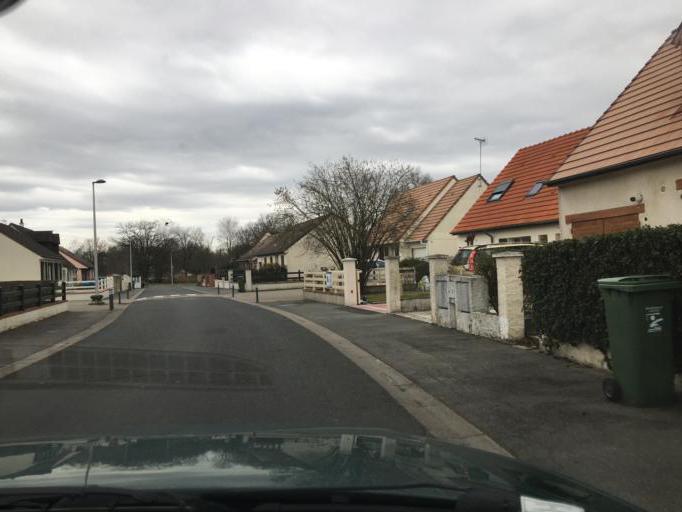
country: FR
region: Centre
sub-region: Departement du Loiret
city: Saran
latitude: 47.9522
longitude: 1.8984
